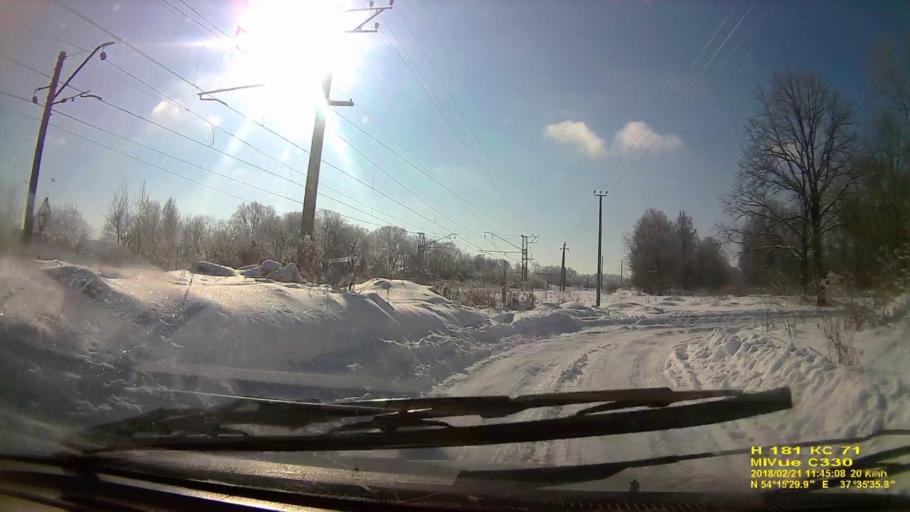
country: RU
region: Tula
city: Gorelki
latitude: 54.2583
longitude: 37.5933
